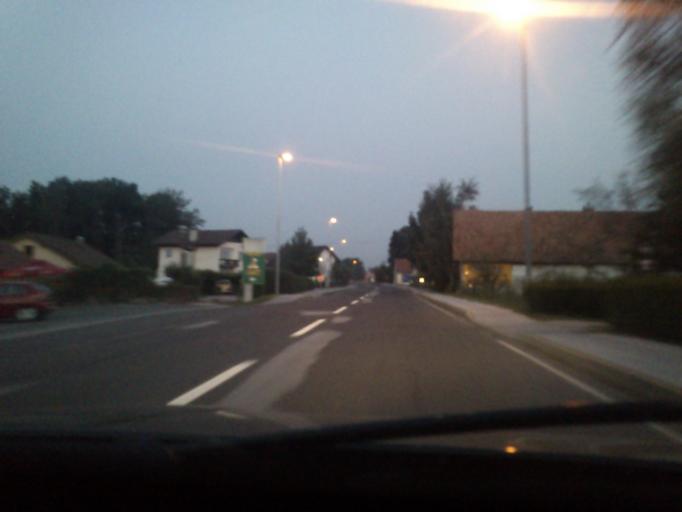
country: SI
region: Hajdina
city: Spodnja Hajdina
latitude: 46.4239
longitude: 15.8289
